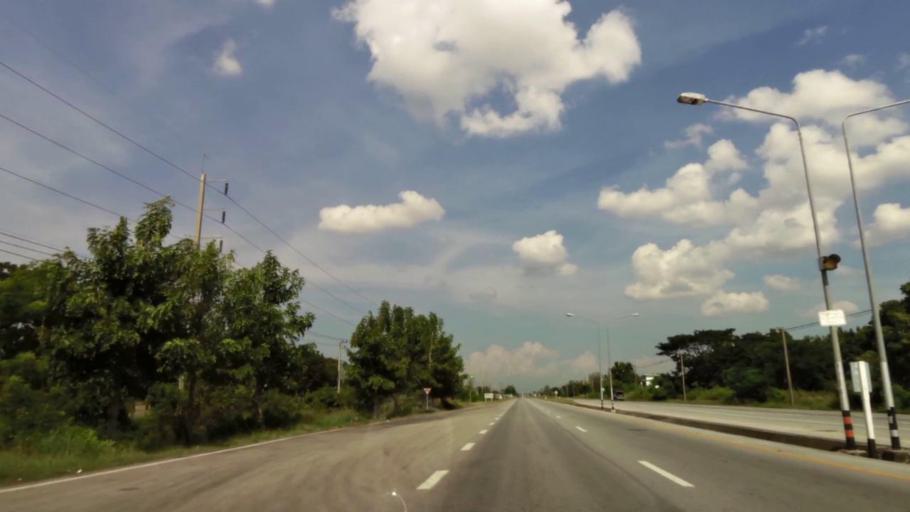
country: TH
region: Uttaradit
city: Thong Saen Khan
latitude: 17.4807
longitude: 100.2349
